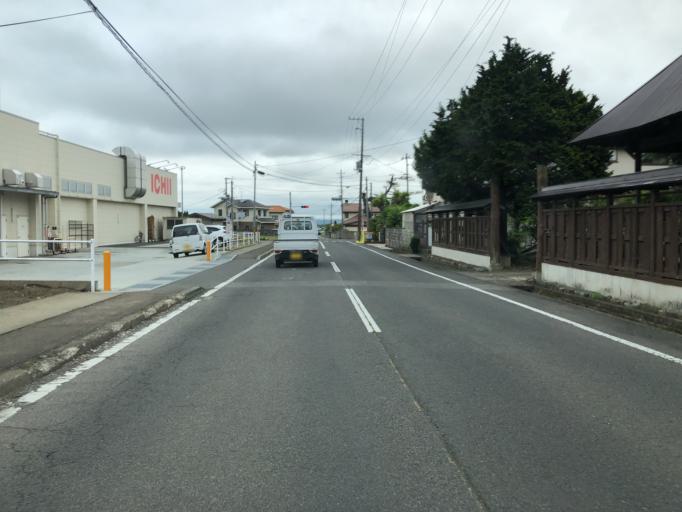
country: JP
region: Fukushima
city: Fukushima-shi
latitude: 37.7677
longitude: 140.3874
